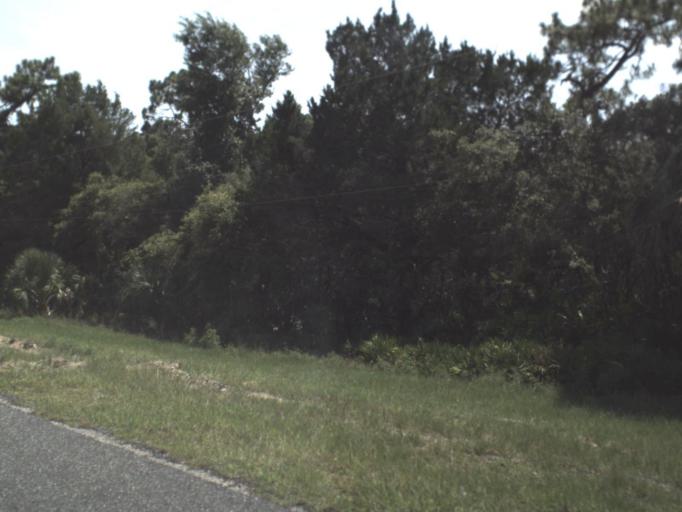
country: US
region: Florida
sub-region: Levy County
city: Inglis
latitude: 29.1175
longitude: -82.6367
